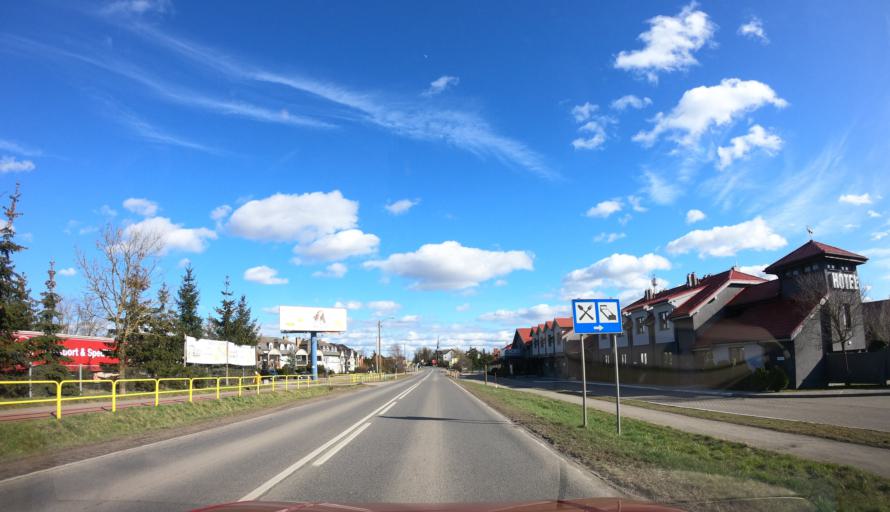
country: PL
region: West Pomeranian Voivodeship
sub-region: Powiat policki
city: Przeclaw
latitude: 53.4319
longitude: 14.4553
